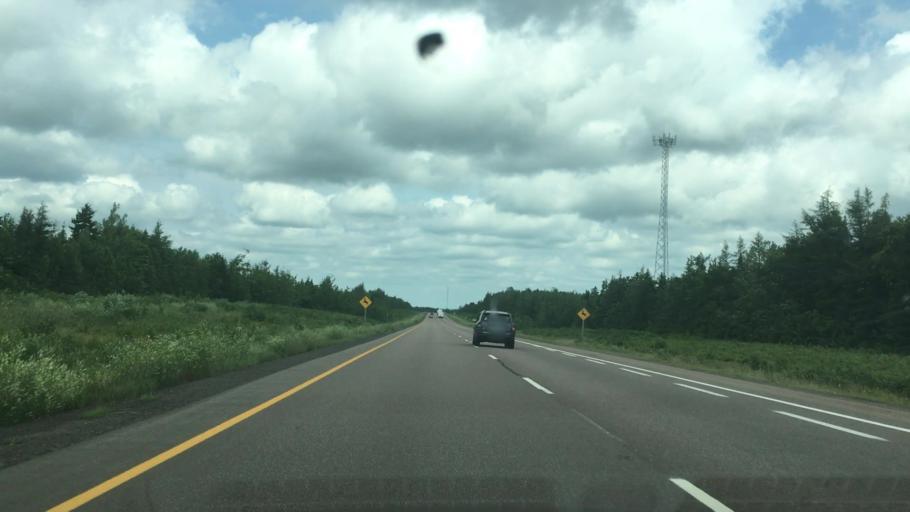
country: CA
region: New Brunswick
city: Dieppe
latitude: 46.0558
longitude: -64.5865
